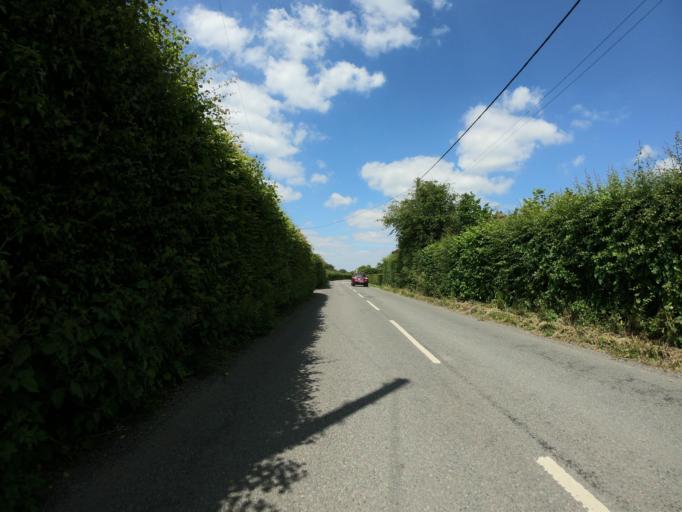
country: GB
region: England
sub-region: Kent
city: Halstead
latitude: 51.3327
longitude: 0.1354
